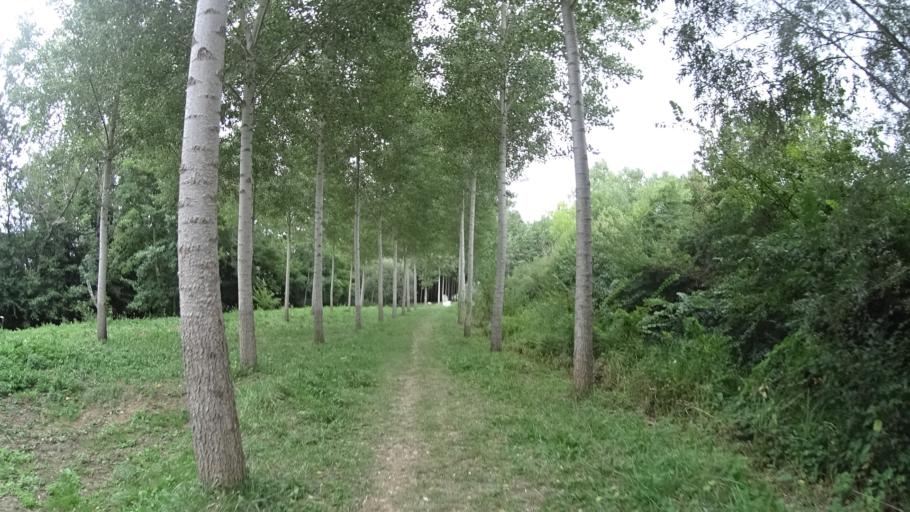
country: FR
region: Centre
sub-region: Departement du Loiret
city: Amilly
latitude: 47.9520
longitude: 2.7830
